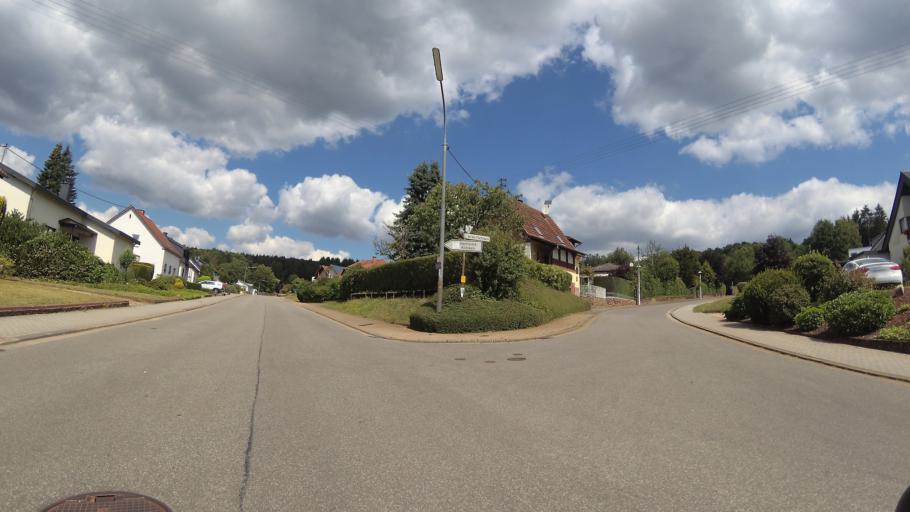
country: DE
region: Saarland
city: Weiskirchen
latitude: 49.5607
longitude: 6.8076
